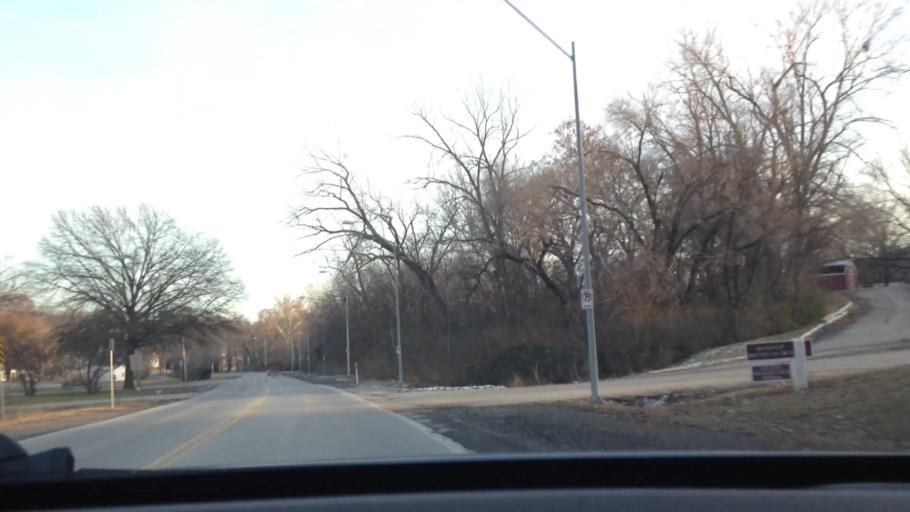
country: US
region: Missouri
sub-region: Clay County
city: North Kansas City
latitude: 39.1651
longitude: -94.5506
